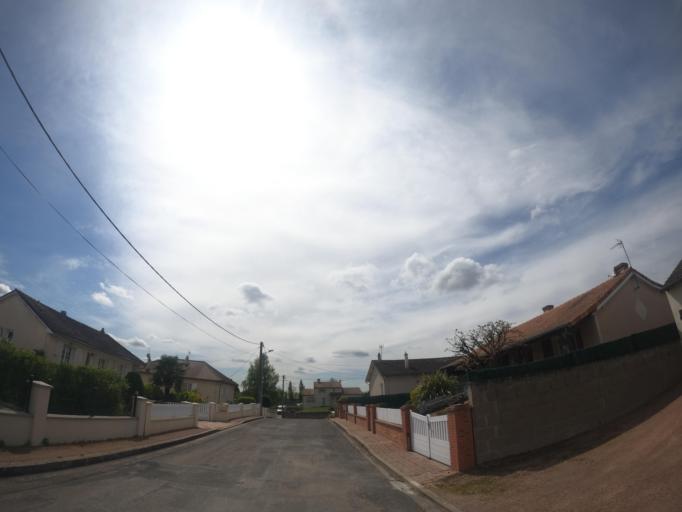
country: FR
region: Poitou-Charentes
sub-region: Departement des Deux-Sevres
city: Saint-Jean-de-Thouars
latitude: 46.9247
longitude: -0.1959
